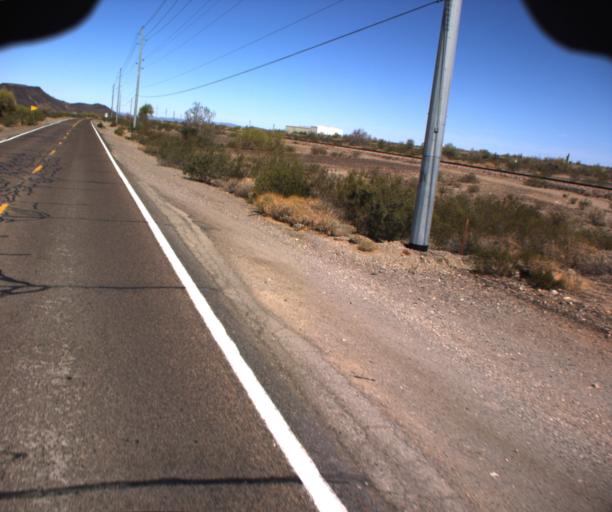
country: US
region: Arizona
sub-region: La Paz County
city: Salome
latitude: 33.7456
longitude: -113.7570
